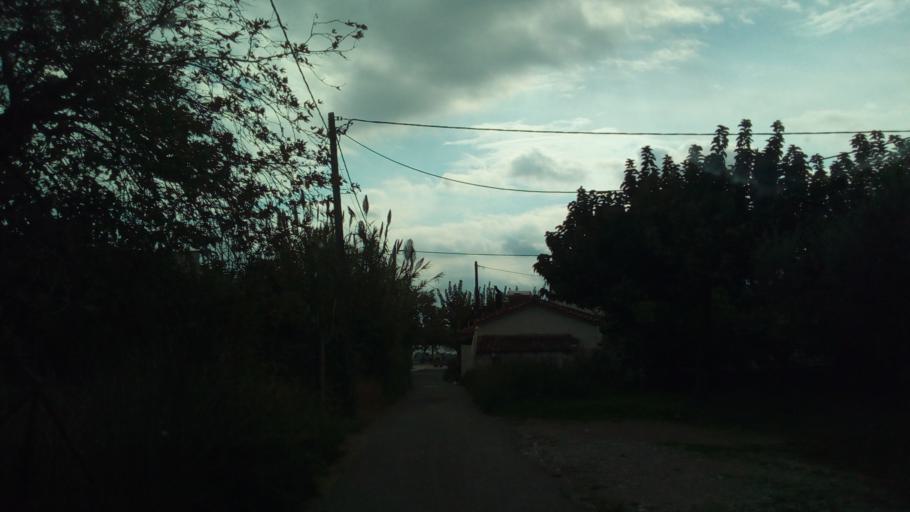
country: GR
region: West Greece
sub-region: Nomos Achaias
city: Kamarai
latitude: 38.3913
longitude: 22.0115
